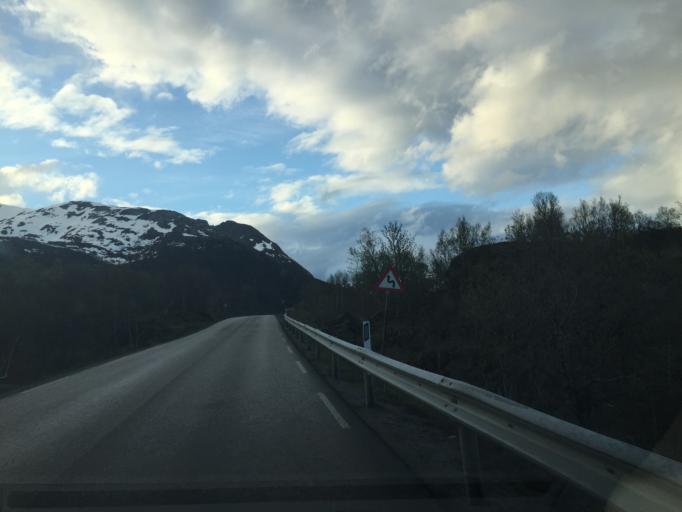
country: NO
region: Nordland
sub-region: Vagan
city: Svolvaer
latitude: 68.3210
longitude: 14.6993
